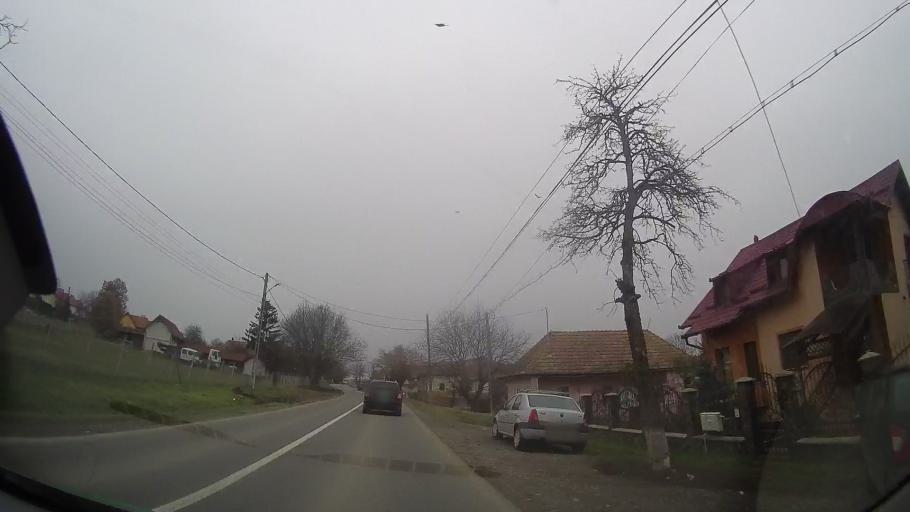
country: RO
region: Mures
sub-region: Comuna Ceausu de Campie
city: Ceausu de Campie
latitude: 46.6086
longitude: 24.5293
